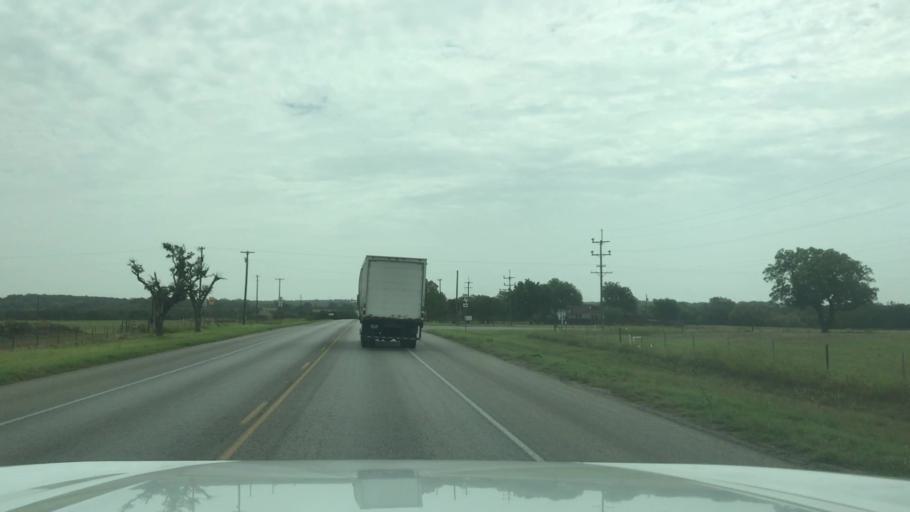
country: US
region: Texas
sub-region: Comanche County
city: De Leon
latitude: 32.0953
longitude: -98.4563
